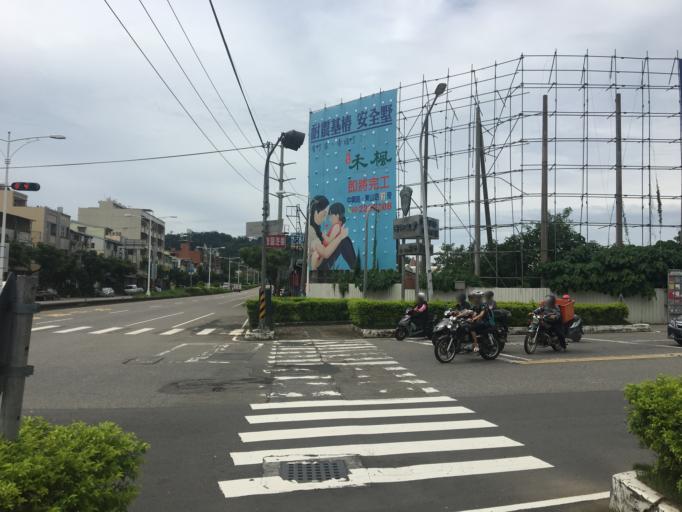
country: TW
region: Taiwan
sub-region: Taichung City
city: Taichung
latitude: 24.0597
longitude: 120.6950
